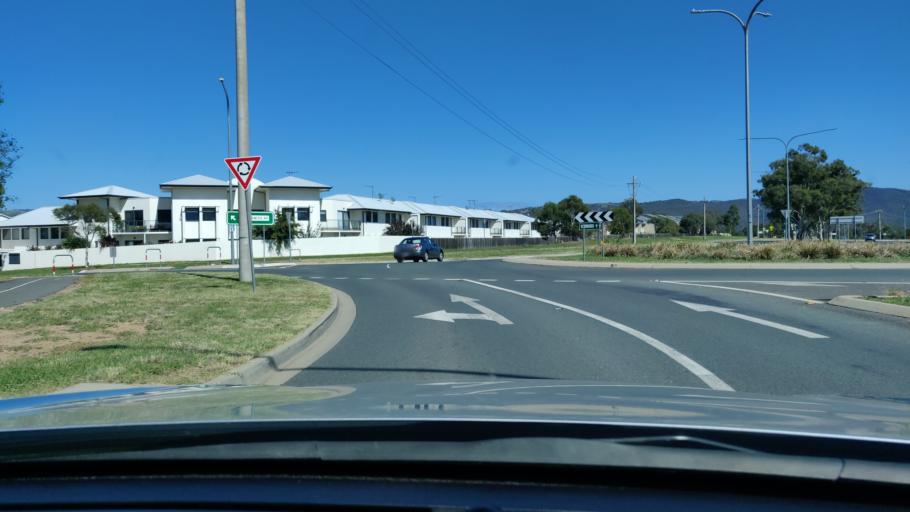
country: AU
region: Australian Capital Territory
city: Macarthur
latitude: -35.4250
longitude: 149.0730
